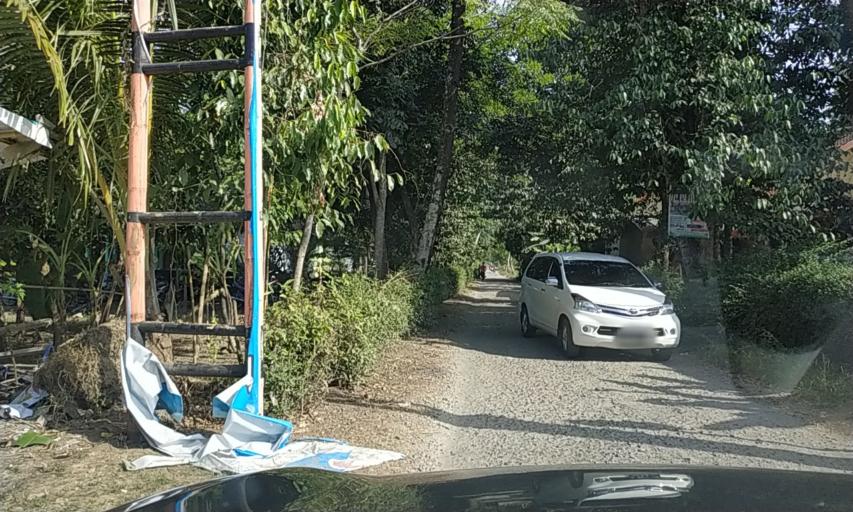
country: ID
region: Central Java
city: Gombong
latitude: -7.7558
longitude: 109.5199
